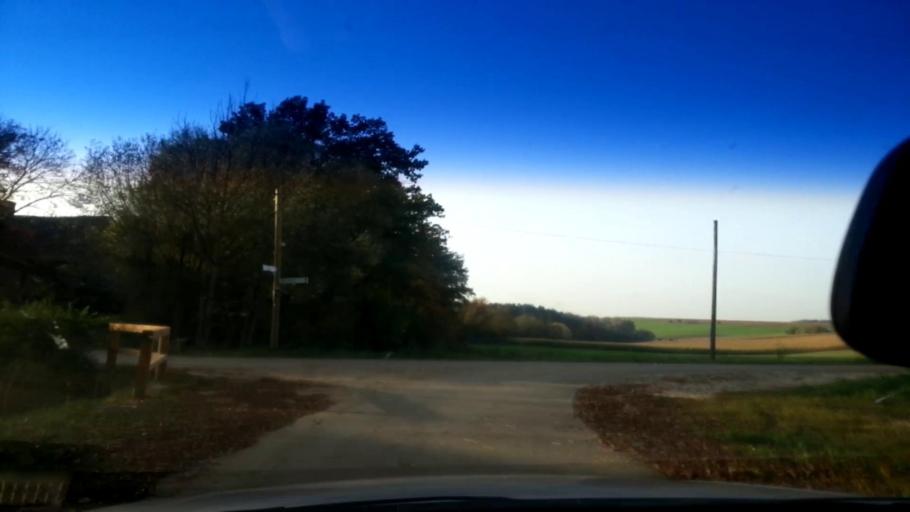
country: DE
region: Bavaria
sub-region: Upper Franconia
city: Ebensfeld
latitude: 50.0209
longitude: 10.9949
